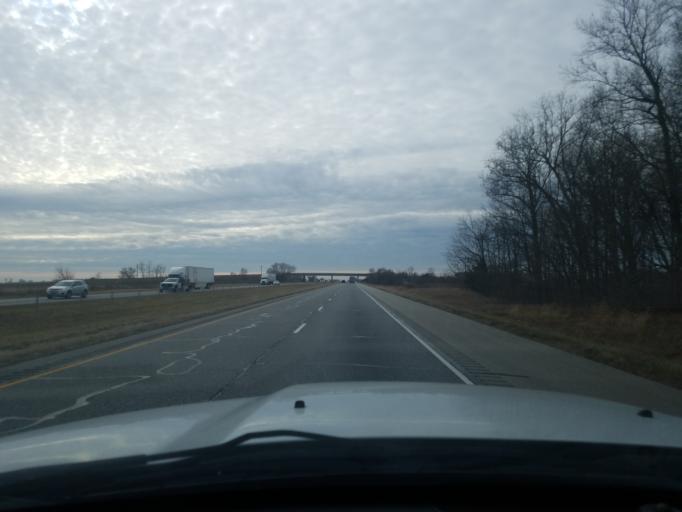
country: US
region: Indiana
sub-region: Huntington County
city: Warren
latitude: 40.6997
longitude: -85.4630
